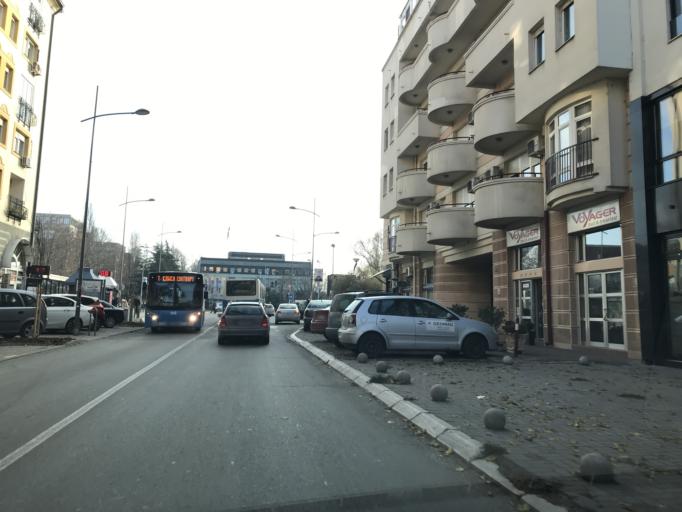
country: RS
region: Autonomna Pokrajina Vojvodina
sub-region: Juznobacki Okrug
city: Novi Sad
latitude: 45.2485
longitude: 19.8488
